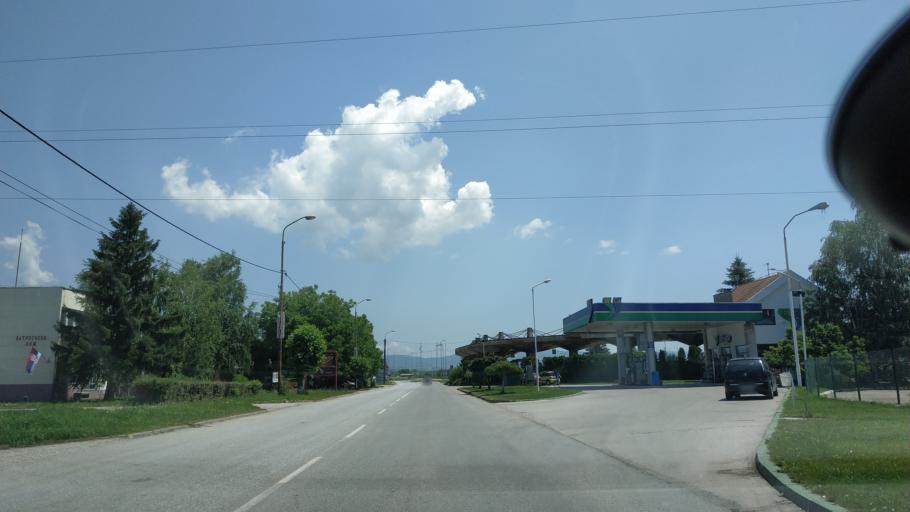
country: RS
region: Central Serbia
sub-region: Pomoravski Okrug
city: Cuprija
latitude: 43.9348
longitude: 21.3847
